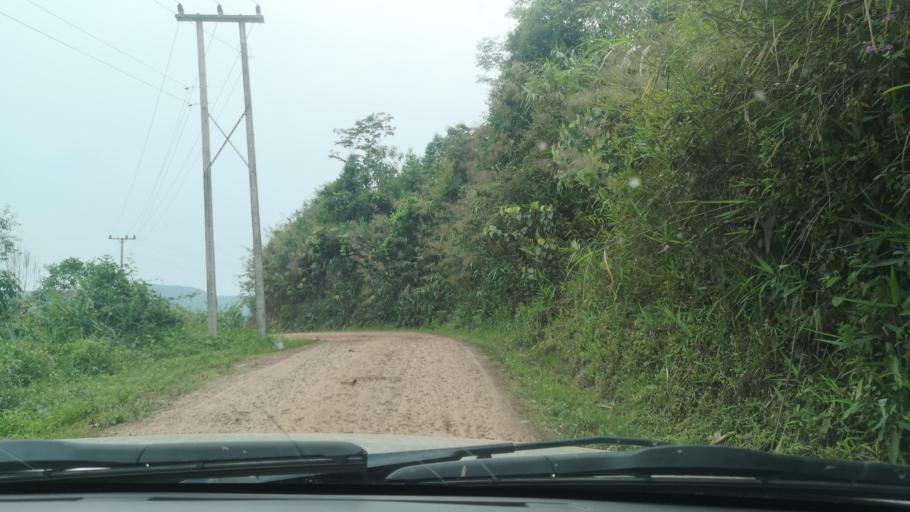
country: LA
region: Oudomxai
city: Muang La
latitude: 21.1264
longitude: 101.8770
